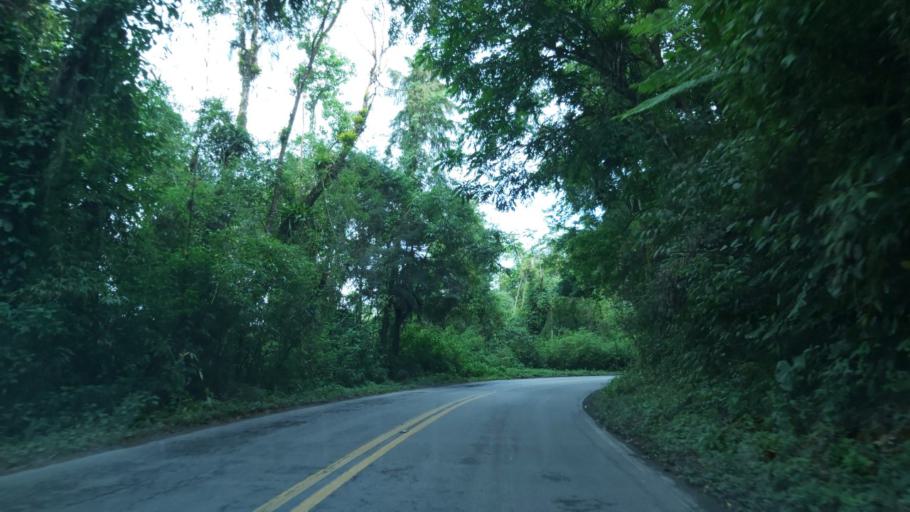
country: BR
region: Sao Paulo
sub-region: Miracatu
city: Miracatu
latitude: -24.0445
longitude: -47.5683
